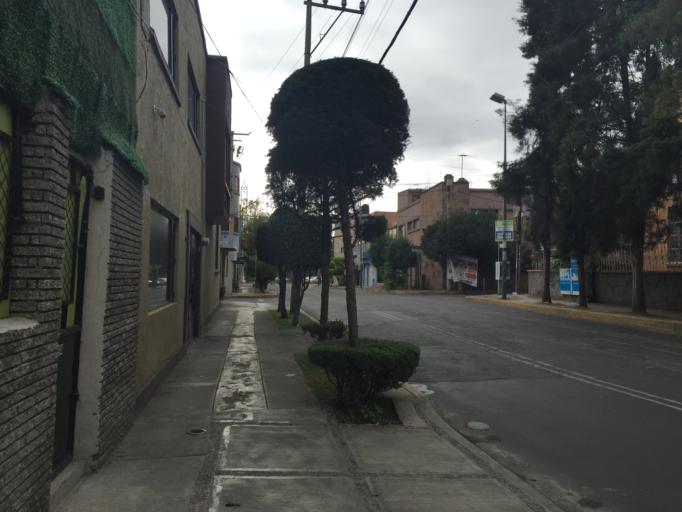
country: MX
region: Mexico
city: Colonia Lindavista
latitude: 19.4849
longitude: -99.1278
